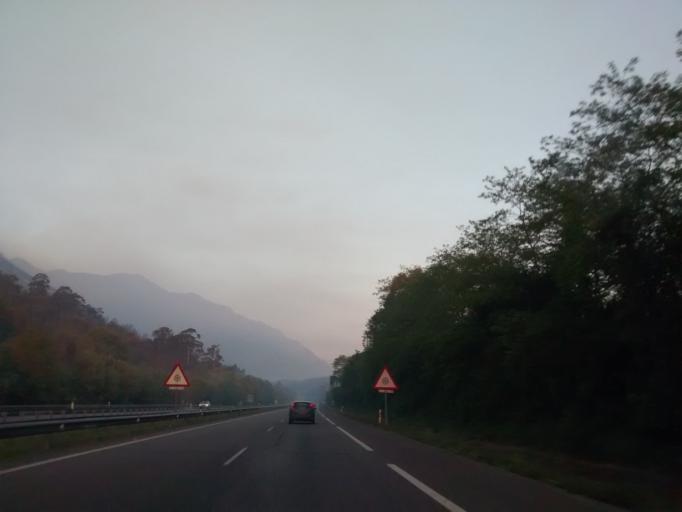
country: ES
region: Asturias
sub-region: Province of Asturias
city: Ribadesella
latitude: 43.4388
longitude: -4.9711
